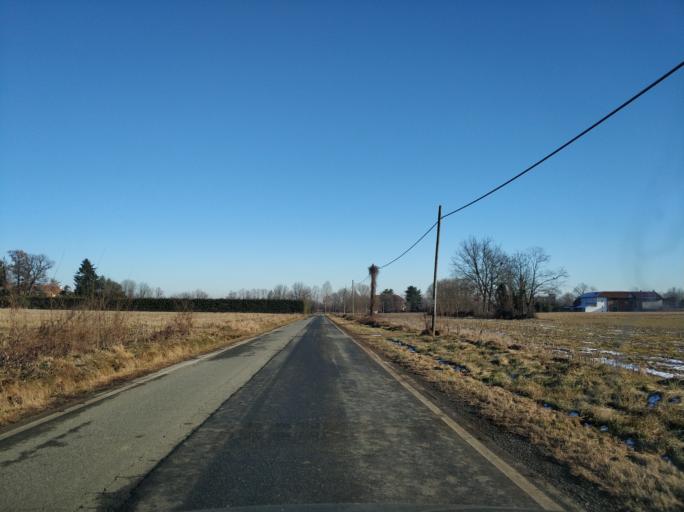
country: IT
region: Piedmont
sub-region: Provincia di Torino
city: San Maurizio
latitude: 45.2410
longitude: 7.6323
